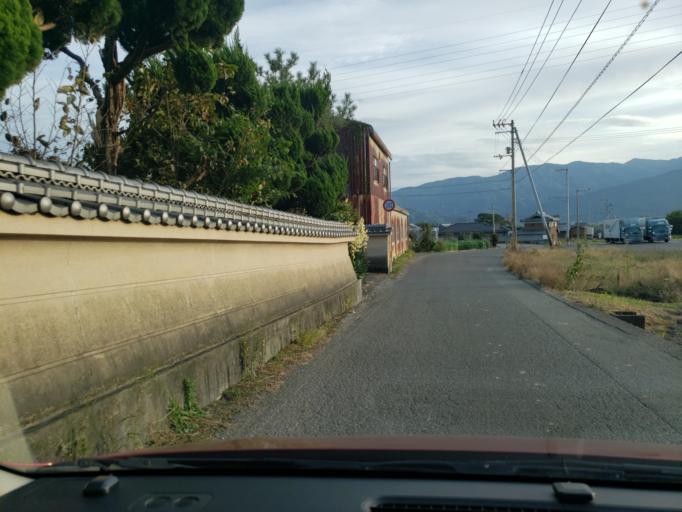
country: JP
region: Tokushima
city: Wakimachi
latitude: 34.0804
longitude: 134.2284
